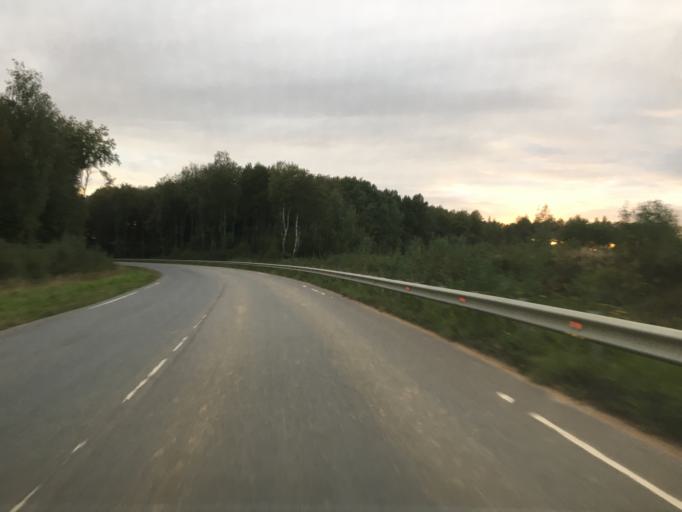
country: RU
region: Kaluga
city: Kaluga
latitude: 54.5872
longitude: 36.3603
